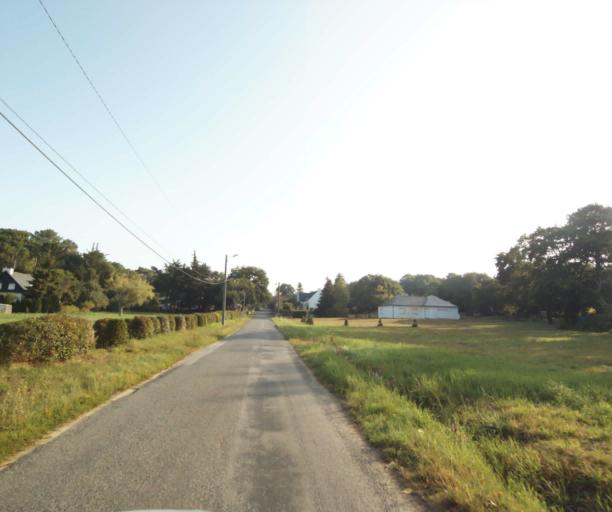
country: FR
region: Brittany
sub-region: Departement du Morbihan
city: Riantec
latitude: 47.7132
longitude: -3.2933
